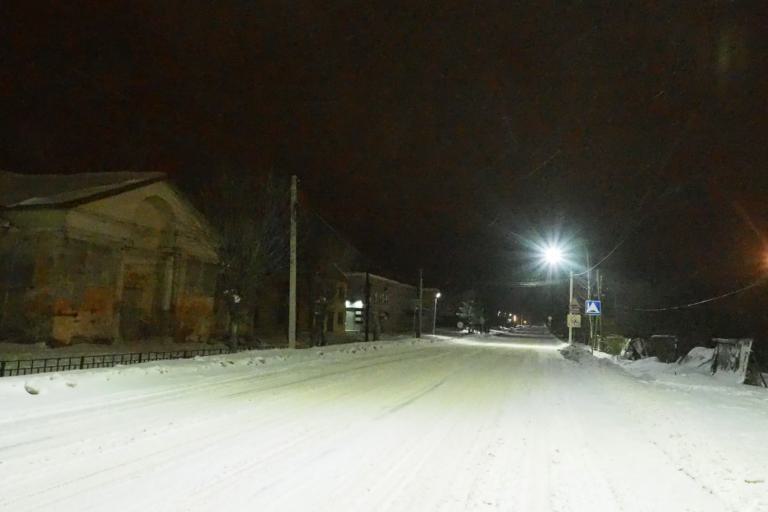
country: RU
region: Tverskaya
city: Sonkovo
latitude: 57.7807
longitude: 37.1657
